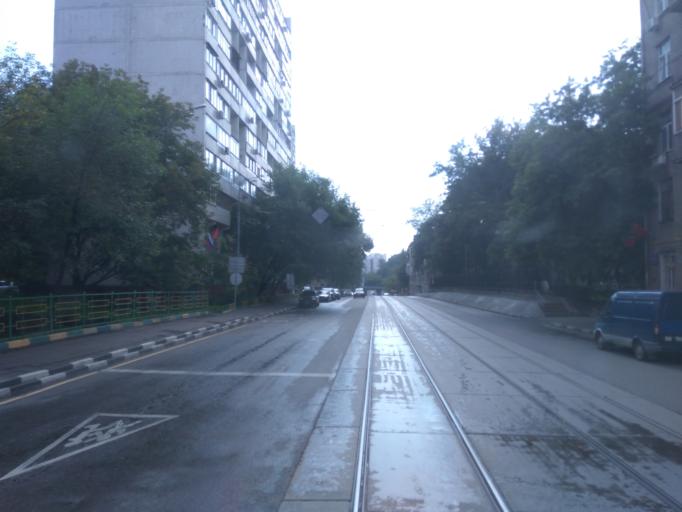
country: RU
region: Moscow
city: Taganskiy
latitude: 55.7523
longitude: 37.6783
